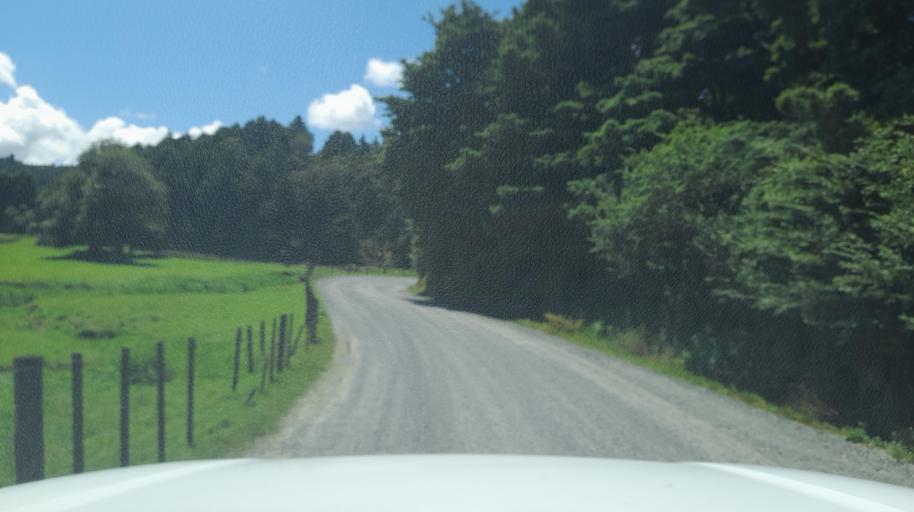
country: NZ
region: Northland
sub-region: Far North District
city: Kaitaia
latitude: -35.1097
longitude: 173.3953
